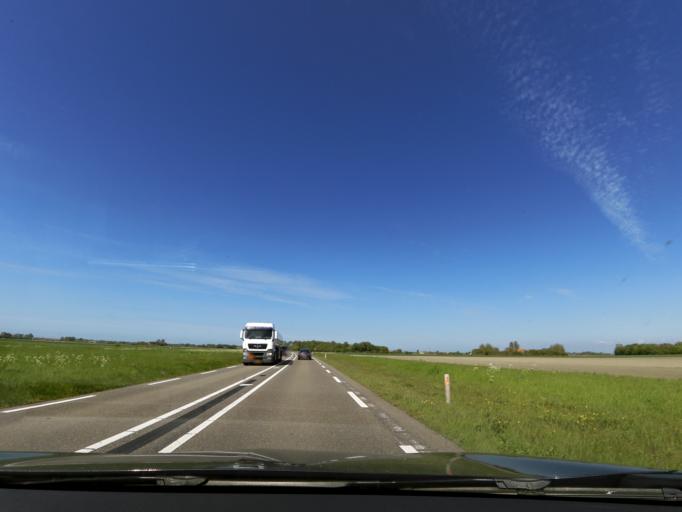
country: NL
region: Zeeland
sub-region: Schouwen-Duiveland
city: Scharendijke
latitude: 51.7097
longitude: 3.8115
